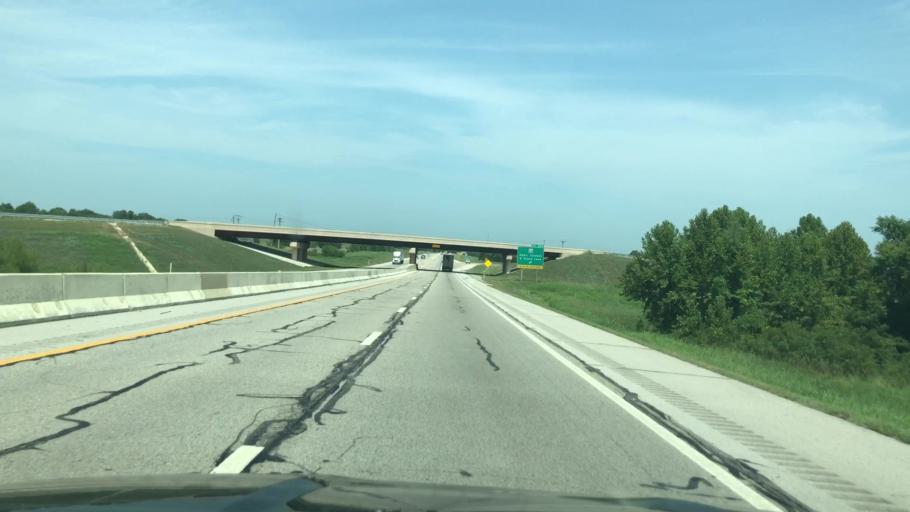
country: US
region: Oklahoma
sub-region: Rogers County
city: Chelsea
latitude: 36.4363
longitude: -95.3830
